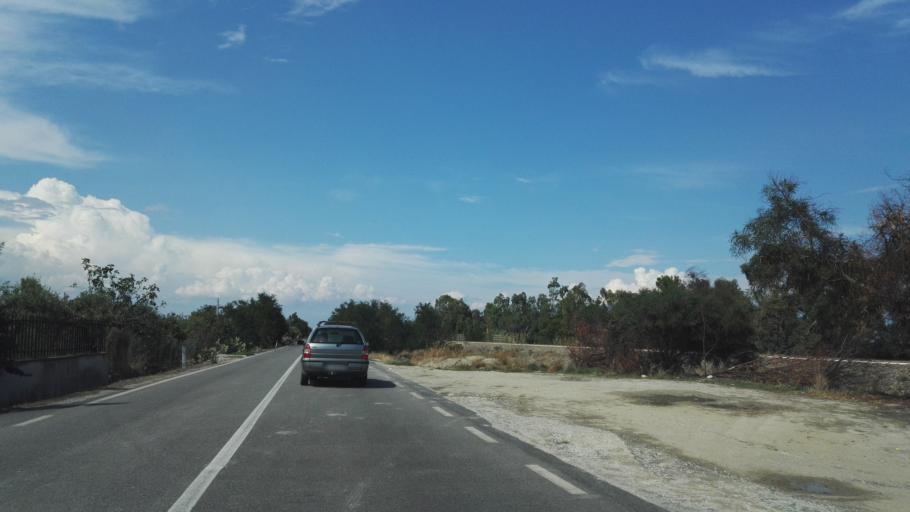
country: IT
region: Calabria
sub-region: Provincia di Catanzaro
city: Santa Caterina dello Ionio Marina
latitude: 38.5507
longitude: 16.5703
